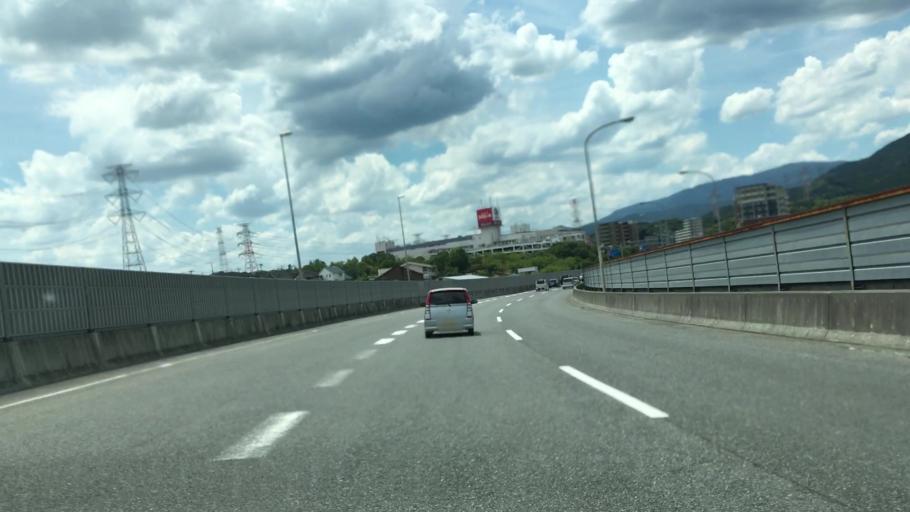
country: JP
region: Fukuoka
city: Chikushino-shi
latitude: 33.4492
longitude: 130.5461
